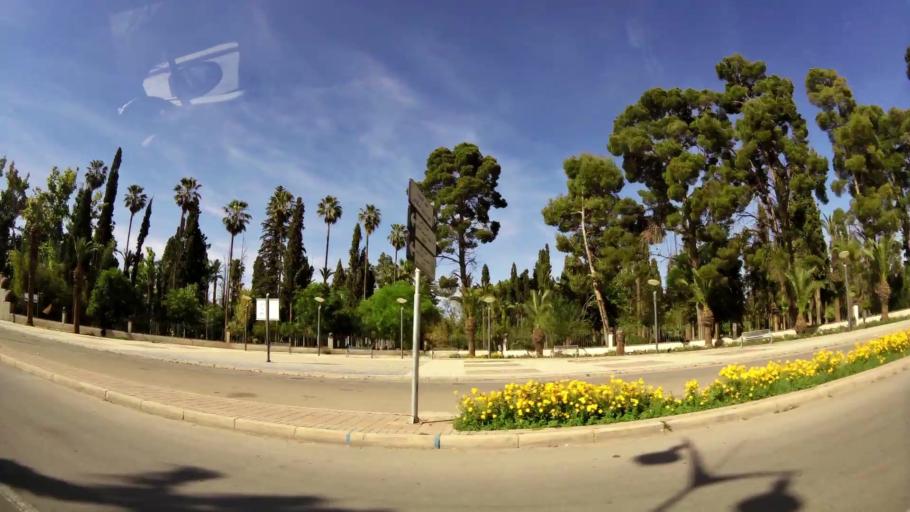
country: MA
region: Oriental
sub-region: Oujda-Angad
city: Oujda
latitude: 34.6711
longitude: -1.9059
